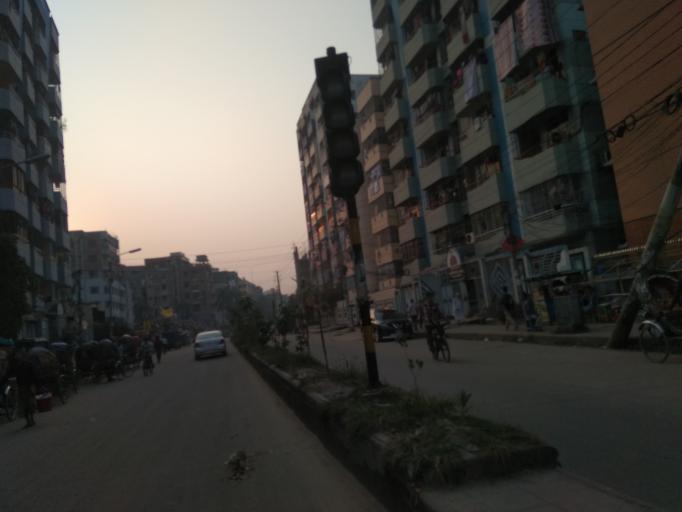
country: BD
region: Dhaka
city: Azimpur
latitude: 23.8104
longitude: 90.3675
